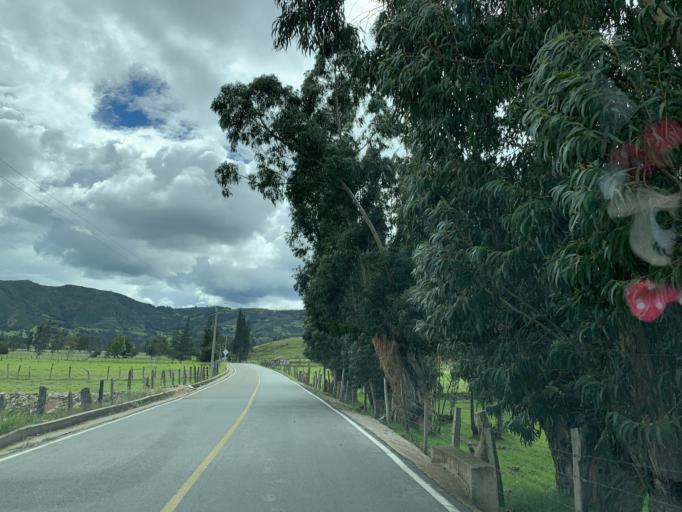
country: CO
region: Boyaca
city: Floresta
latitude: 5.8542
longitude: -72.9317
